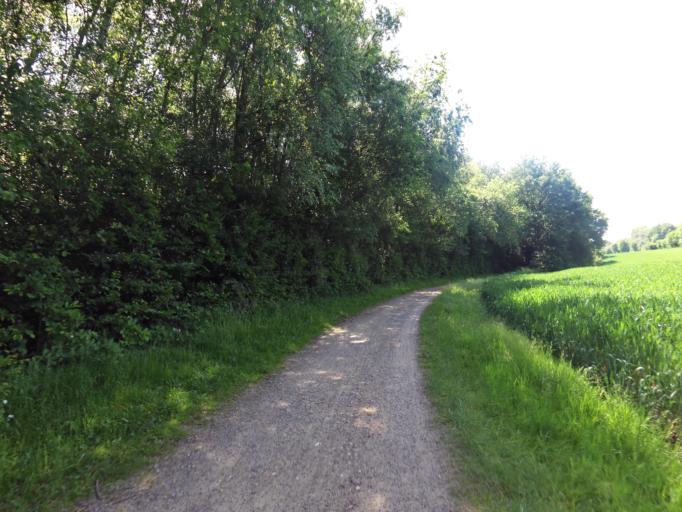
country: DE
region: North Rhine-Westphalia
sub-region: Regierungsbezirk Koln
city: Herzogenrath
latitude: 50.9033
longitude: 6.0827
